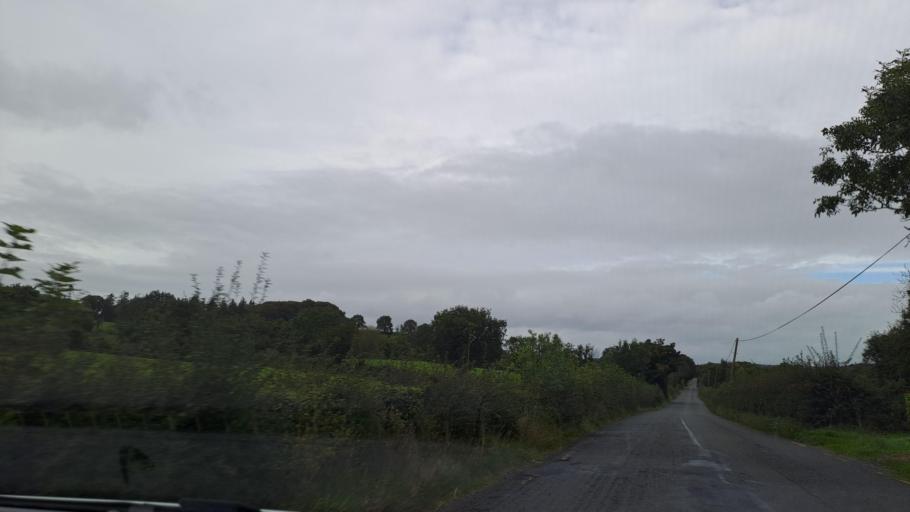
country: IE
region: Ulster
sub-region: An Cabhan
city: Bailieborough
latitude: 54.0332
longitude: -6.8988
